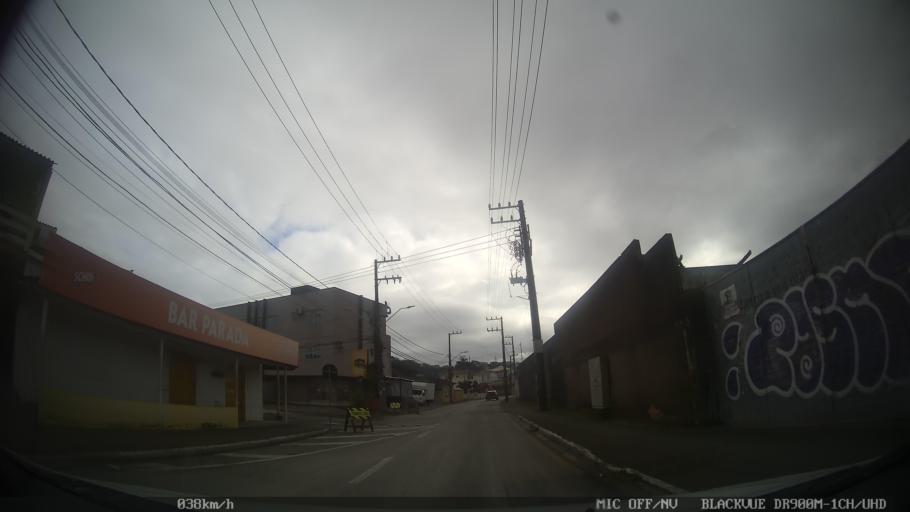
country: BR
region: Santa Catarina
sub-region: Sao Jose
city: Campinas
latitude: -27.5966
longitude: -48.6233
